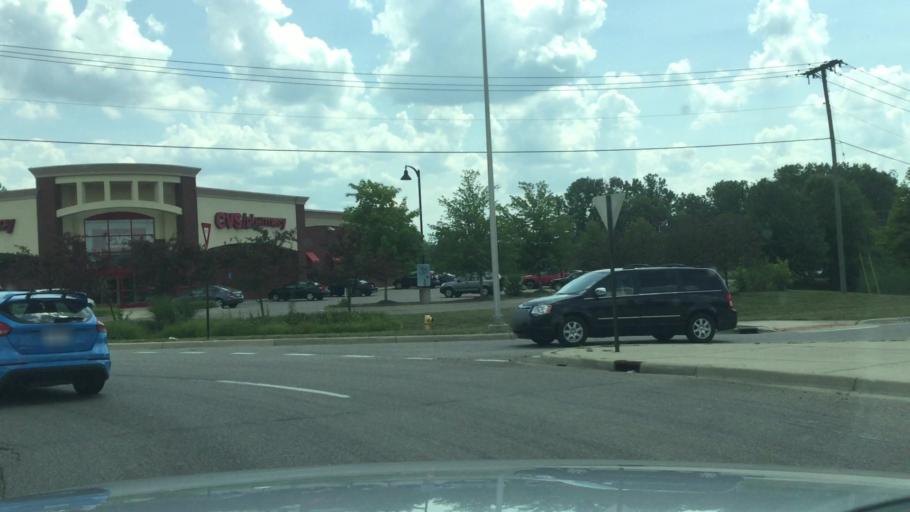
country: US
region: Michigan
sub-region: Washtenaw County
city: Ypsilanti
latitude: 42.2101
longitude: -83.6195
